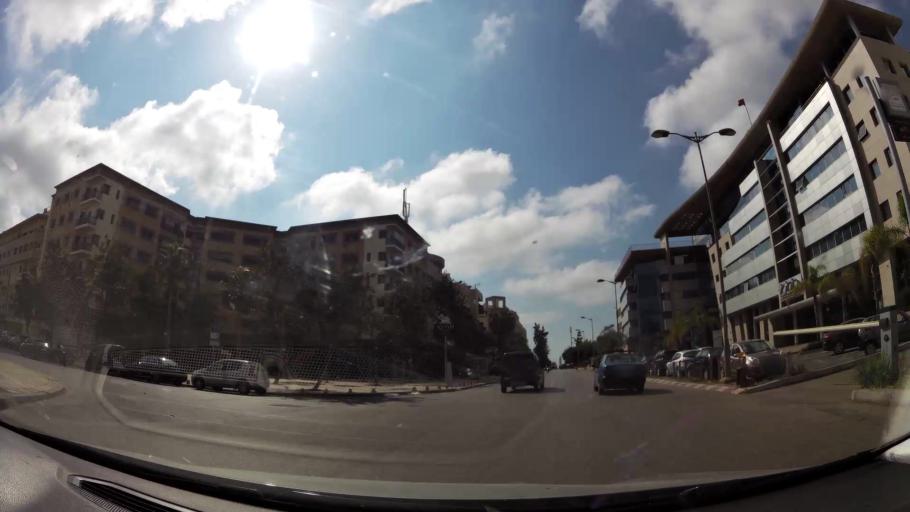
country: MA
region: Rabat-Sale-Zemmour-Zaer
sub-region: Skhirate-Temara
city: Temara
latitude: 33.9543
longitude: -6.8739
